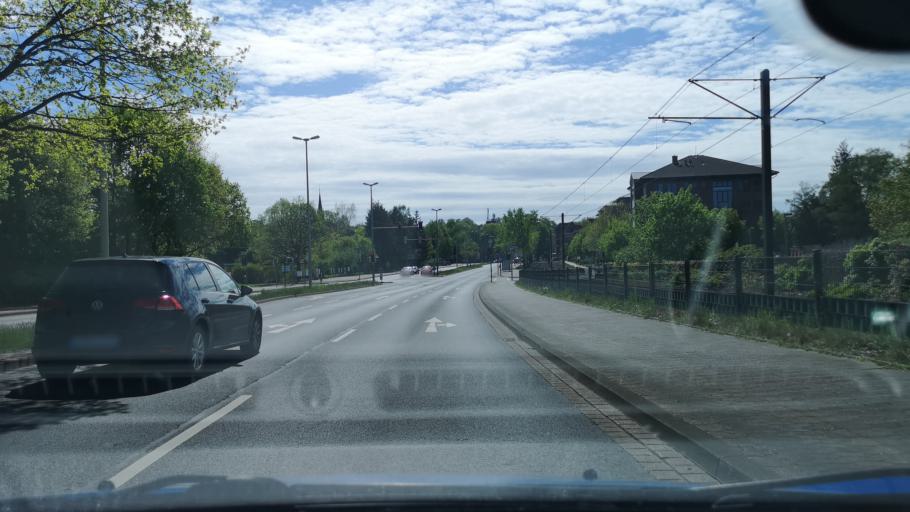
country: DE
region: Lower Saxony
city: Laatzen
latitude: 52.3727
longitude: 9.8070
